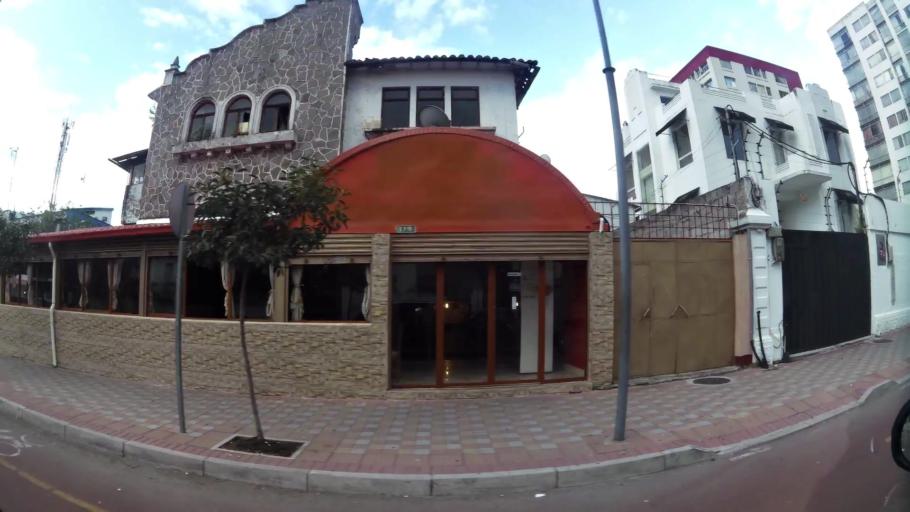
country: EC
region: Pichincha
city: Quito
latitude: -0.2053
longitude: -78.4931
